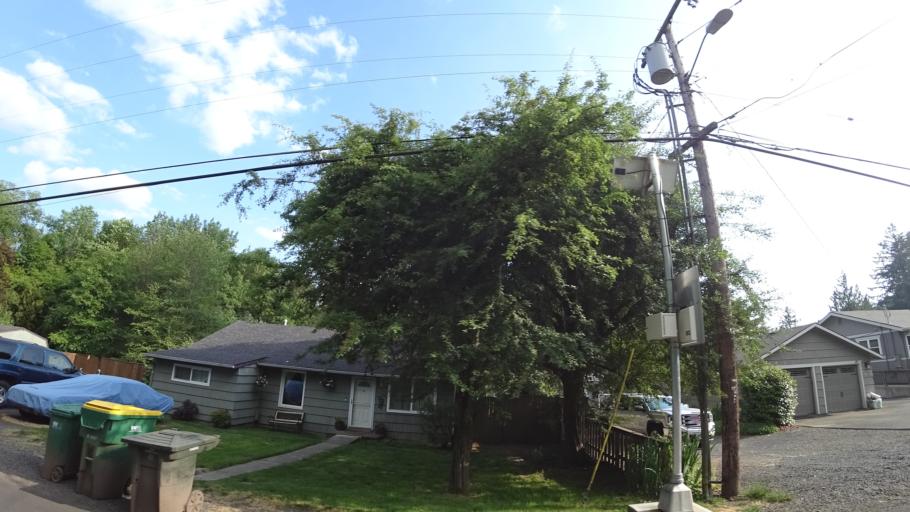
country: US
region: Oregon
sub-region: Washington County
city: Garden Home-Whitford
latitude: 45.4604
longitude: -122.7512
